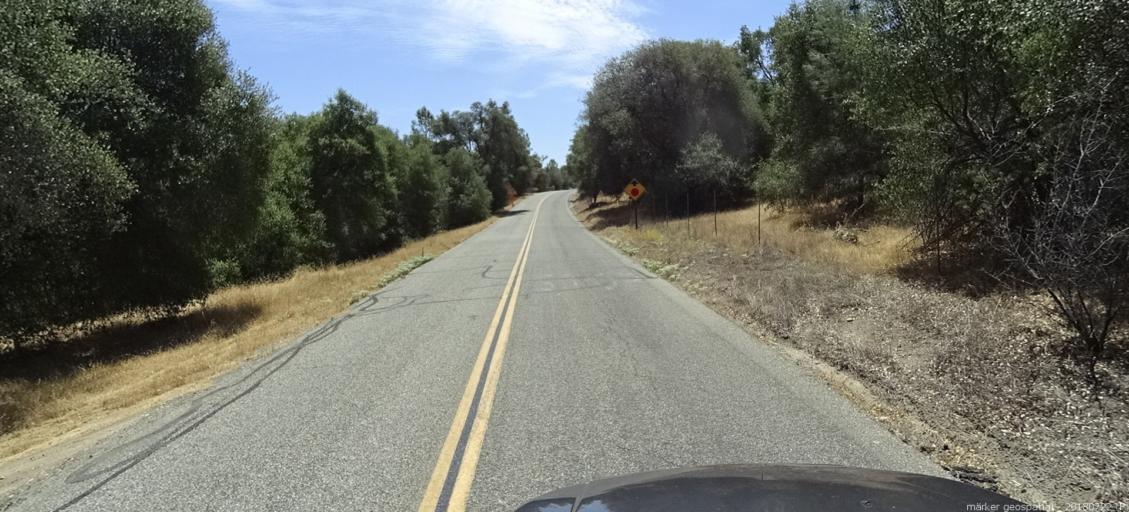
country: US
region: California
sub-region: Madera County
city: Coarsegold
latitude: 37.2570
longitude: -119.7351
